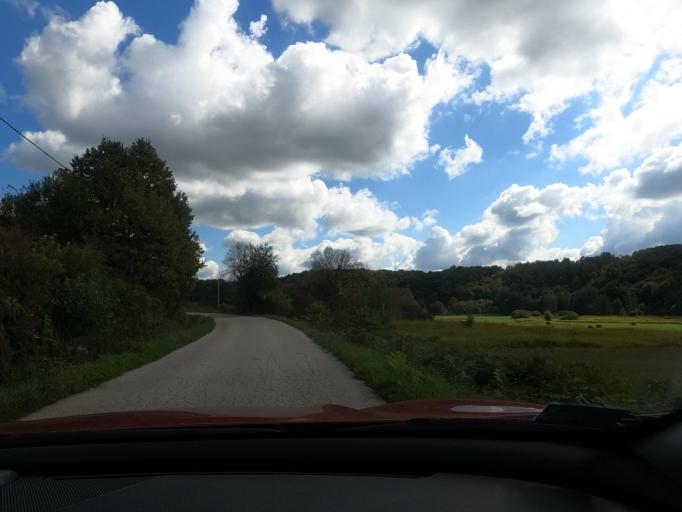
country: BA
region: Federation of Bosnia and Herzegovina
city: Velika Kladusa
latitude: 45.2127
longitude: 15.7209
